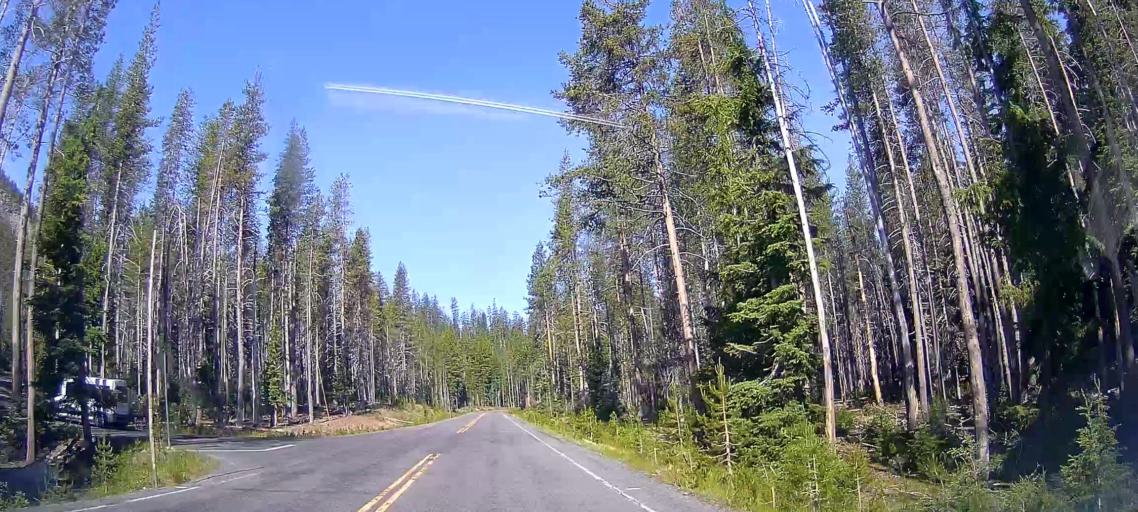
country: US
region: Oregon
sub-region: Jackson County
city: Shady Cove
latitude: 42.8604
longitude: -122.1607
